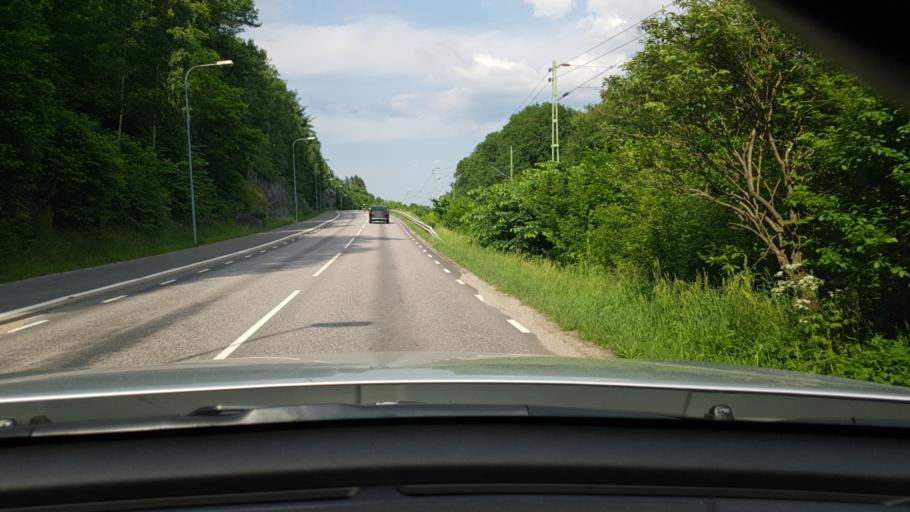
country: SE
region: Vaestra Goetaland
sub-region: Lerums Kommun
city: Stenkullen
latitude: 57.8047
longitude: 12.3495
